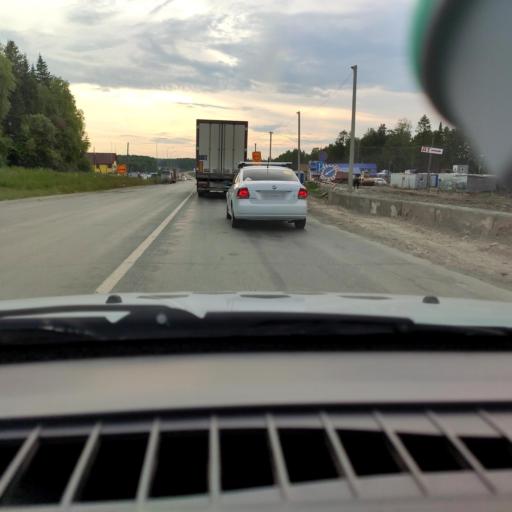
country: RU
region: Sverdlovsk
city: Bisert'
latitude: 56.8296
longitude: 59.0495
